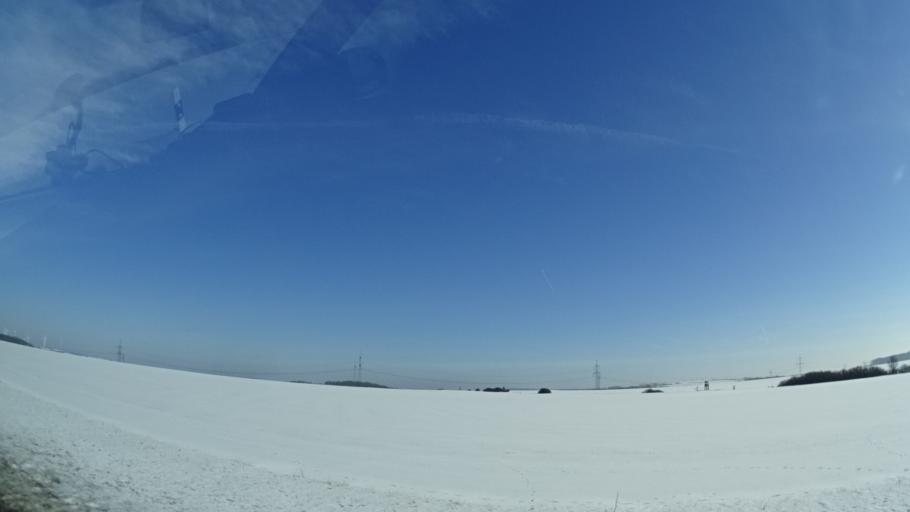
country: DE
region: Thuringia
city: Milda
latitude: 50.8689
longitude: 11.4589
